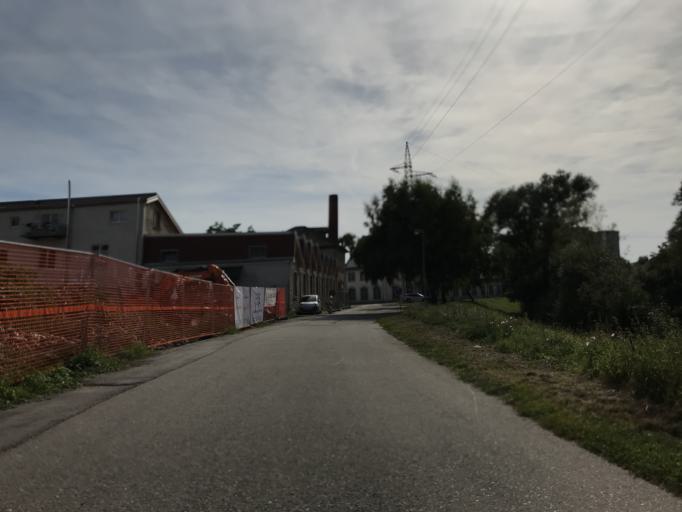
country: DE
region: Baden-Wuerttemberg
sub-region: Freiburg Region
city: Schopfheim
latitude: 47.6546
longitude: 7.8279
